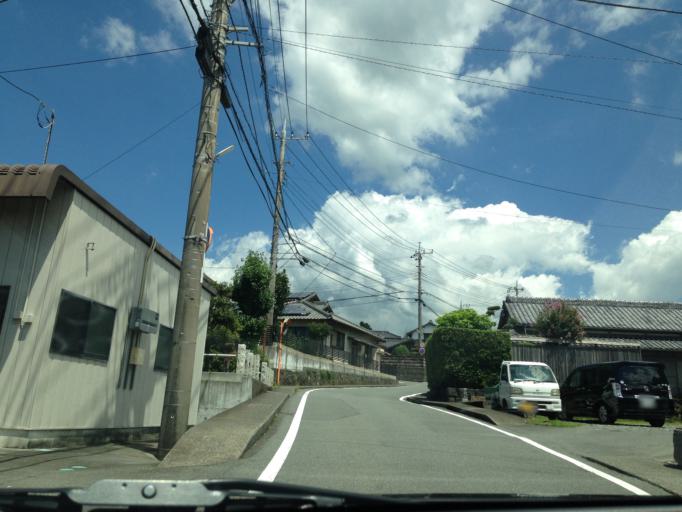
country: JP
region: Shizuoka
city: Fuji
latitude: 35.1938
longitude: 138.7127
